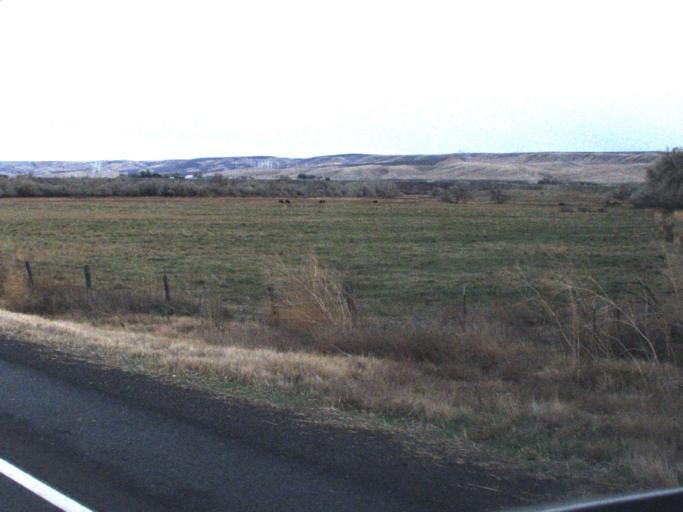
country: US
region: Washington
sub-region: Walla Walla County
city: Garrett
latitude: 46.0477
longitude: -118.6997
